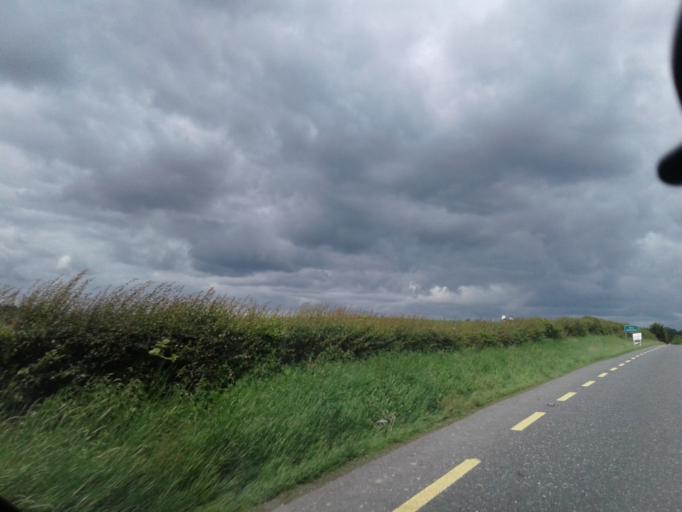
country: IE
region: Leinster
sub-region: Uibh Fhaili
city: Tullamore
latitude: 53.3116
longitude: -7.5028
